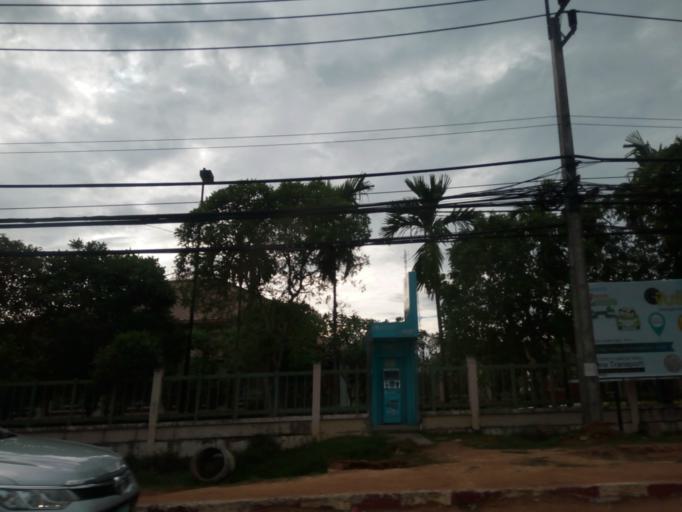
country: TH
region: Phuket
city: Thalang
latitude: 8.1015
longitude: 98.3071
